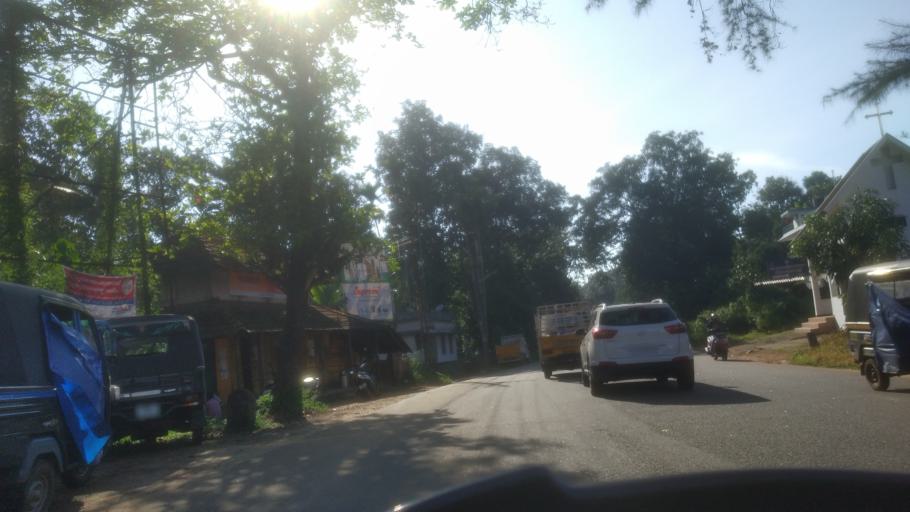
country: IN
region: Kerala
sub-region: Ernakulam
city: Muvattupuzha
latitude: 9.9763
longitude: 76.5325
